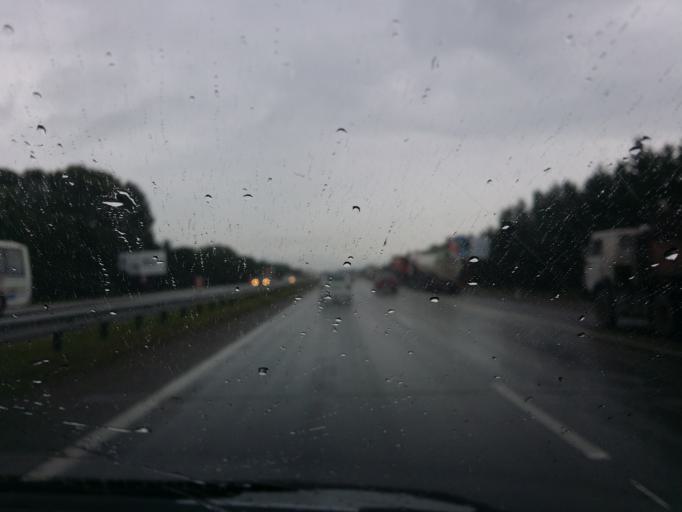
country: RU
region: Altai Krai
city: Zaton
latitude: 53.3151
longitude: 83.8424
